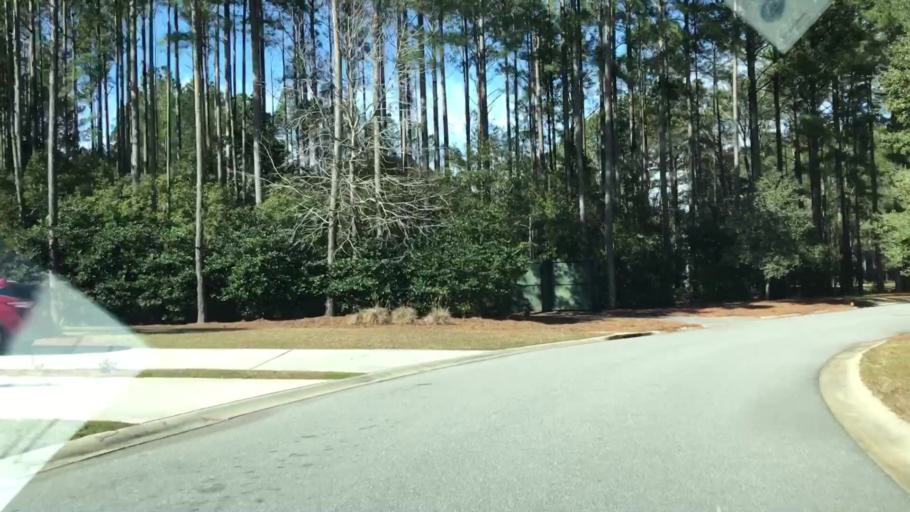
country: US
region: South Carolina
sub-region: Beaufort County
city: Bluffton
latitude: 32.2464
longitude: -80.9311
